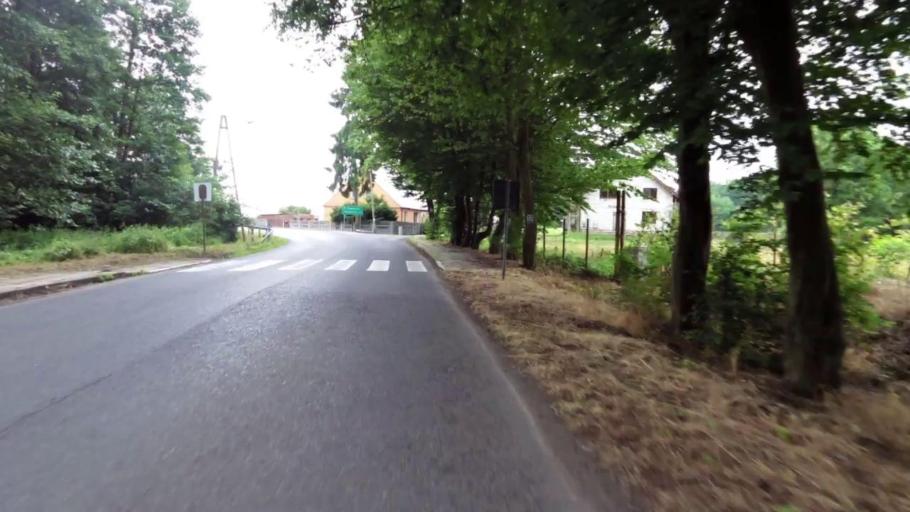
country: PL
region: West Pomeranian Voivodeship
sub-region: Powiat kamienski
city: Wolin
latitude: 53.8358
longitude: 14.6255
